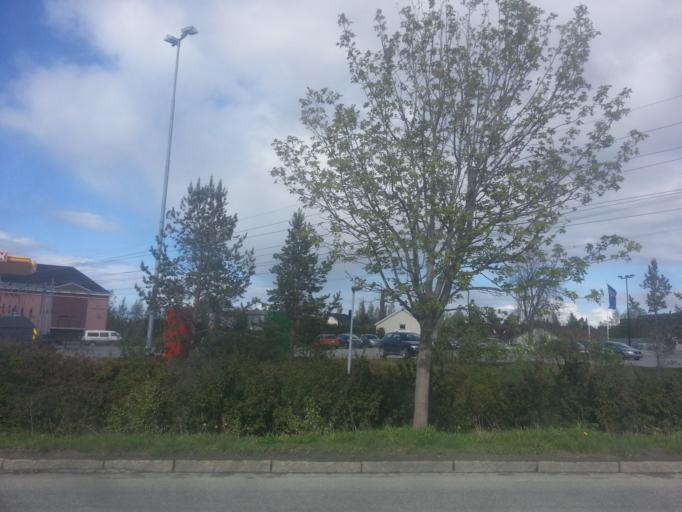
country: NO
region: Sor-Trondelag
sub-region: Trondheim
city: Trondheim
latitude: 63.4100
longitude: 10.4365
